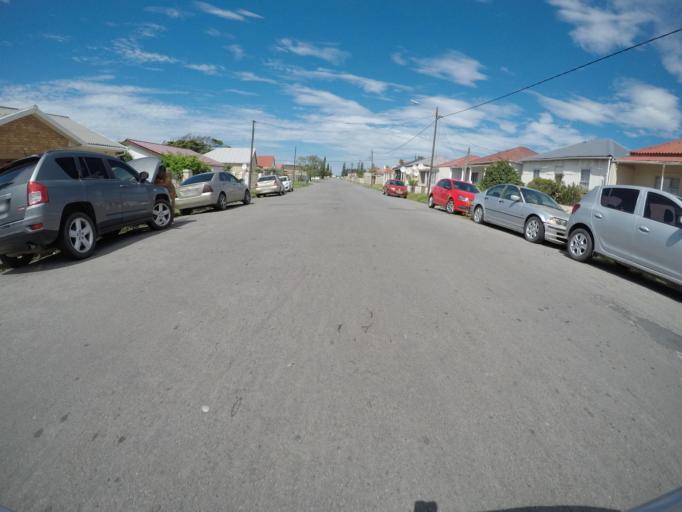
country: ZA
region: Eastern Cape
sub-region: Buffalo City Metropolitan Municipality
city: East London
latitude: -33.0352
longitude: 27.9054
